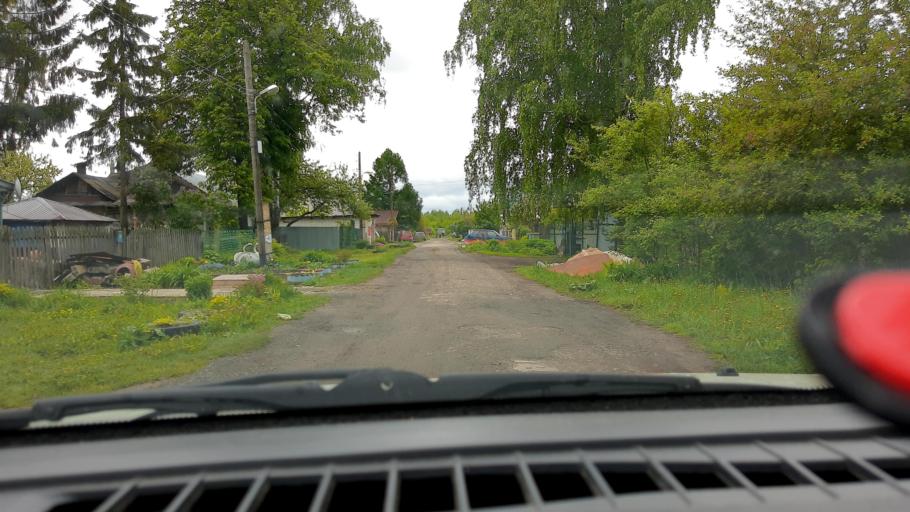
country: RU
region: Nizjnij Novgorod
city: Nizhniy Novgorod
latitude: 56.3075
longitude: 43.8999
